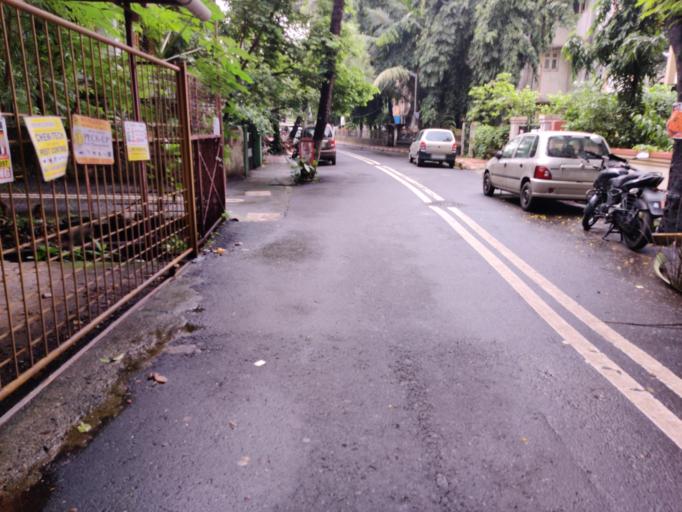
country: IN
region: Maharashtra
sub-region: Mumbai Suburban
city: Borivli
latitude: 19.2522
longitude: 72.8576
